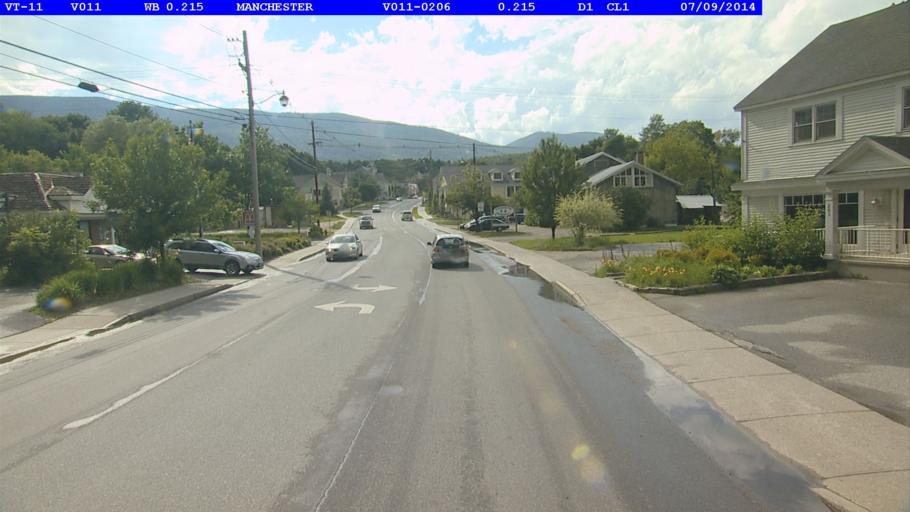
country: US
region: Vermont
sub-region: Bennington County
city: Manchester Center
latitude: 43.1751
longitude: -73.0535
